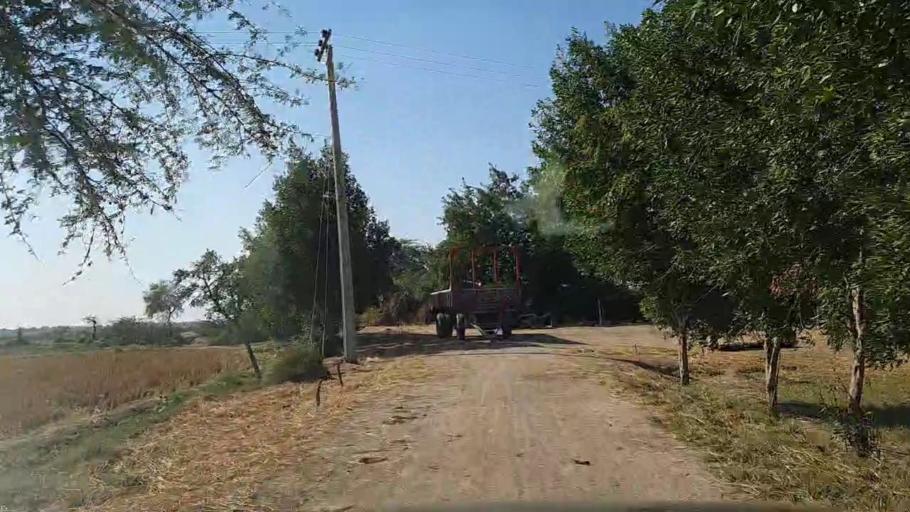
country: PK
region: Sindh
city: Mirpur Batoro
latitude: 24.7159
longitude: 68.2330
